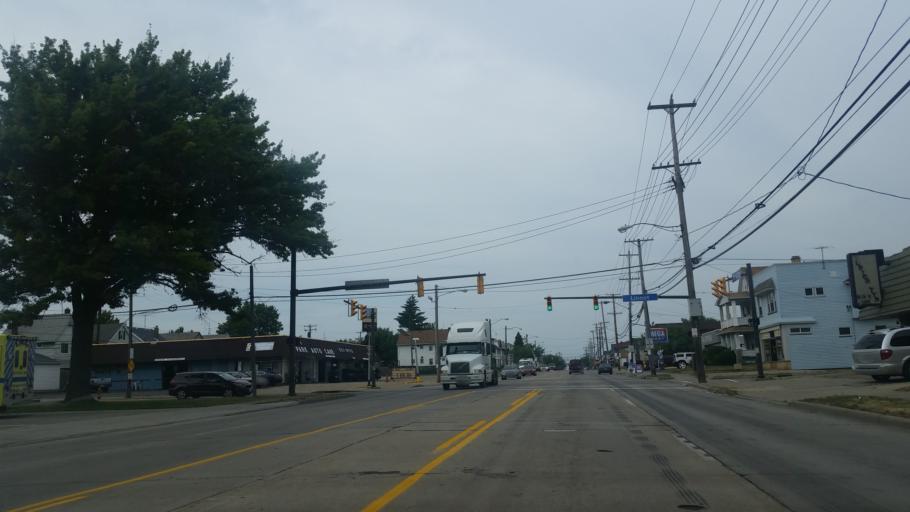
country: US
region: Ohio
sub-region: Cuyahoga County
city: Brooklyn
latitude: 41.4558
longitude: -81.7689
